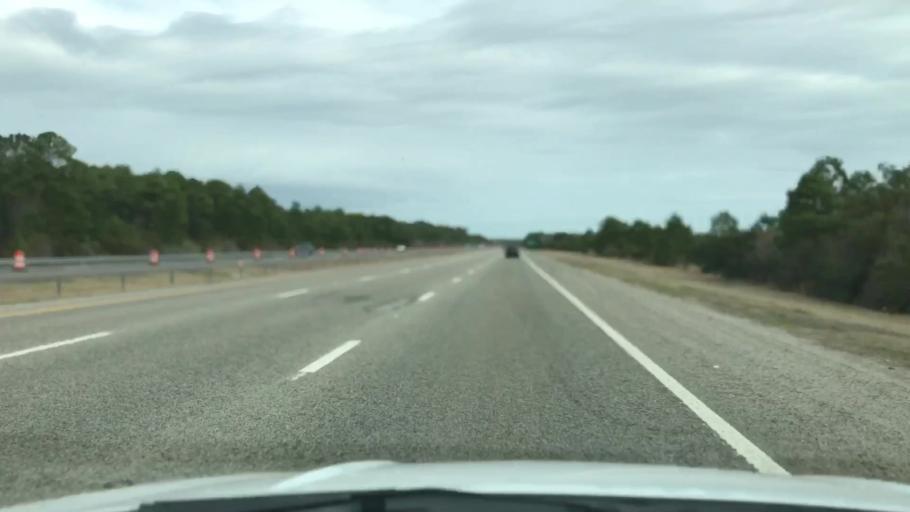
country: US
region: South Carolina
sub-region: Horry County
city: Socastee
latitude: 33.7125
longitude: -79.0059
